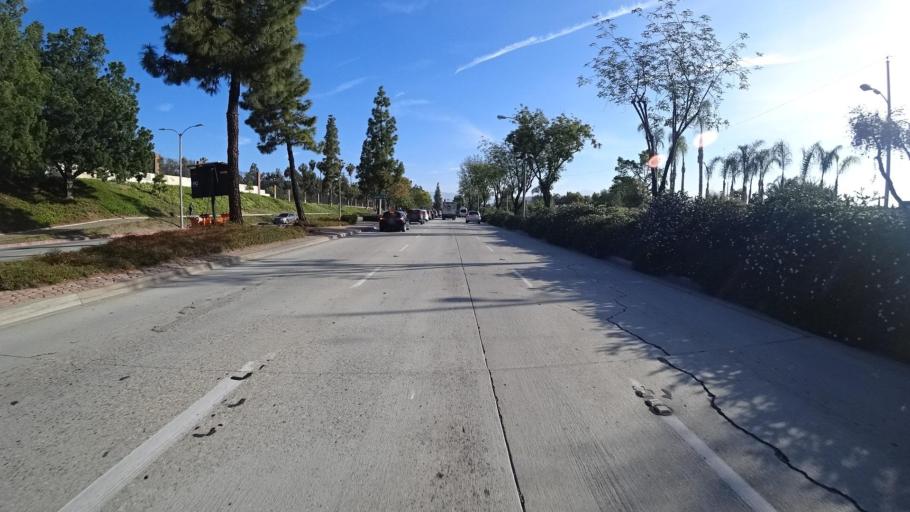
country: US
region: California
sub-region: Los Angeles County
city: South San Jose Hills
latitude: 34.0173
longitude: -117.9205
